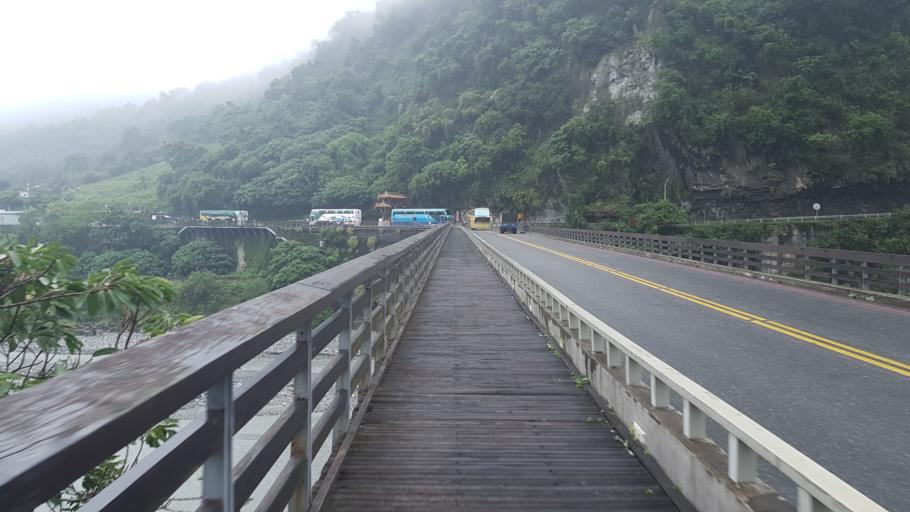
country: TW
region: Taiwan
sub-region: Hualien
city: Hualian
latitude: 24.1567
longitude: 121.6221
